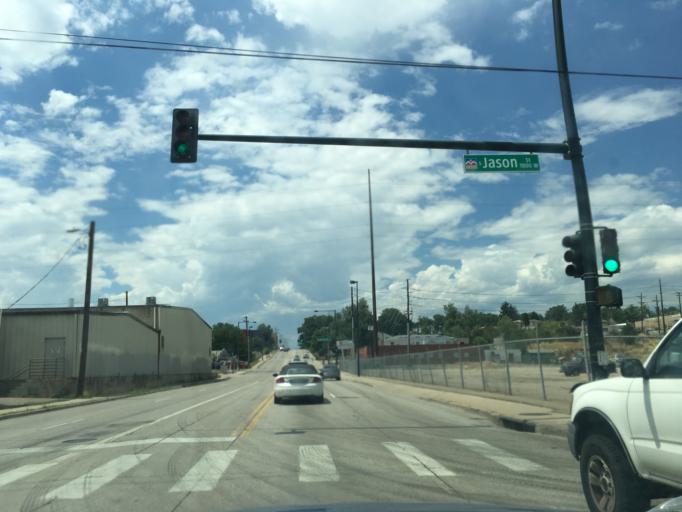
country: US
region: Colorado
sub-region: Denver County
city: Denver
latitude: 39.6967
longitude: -104.9991
